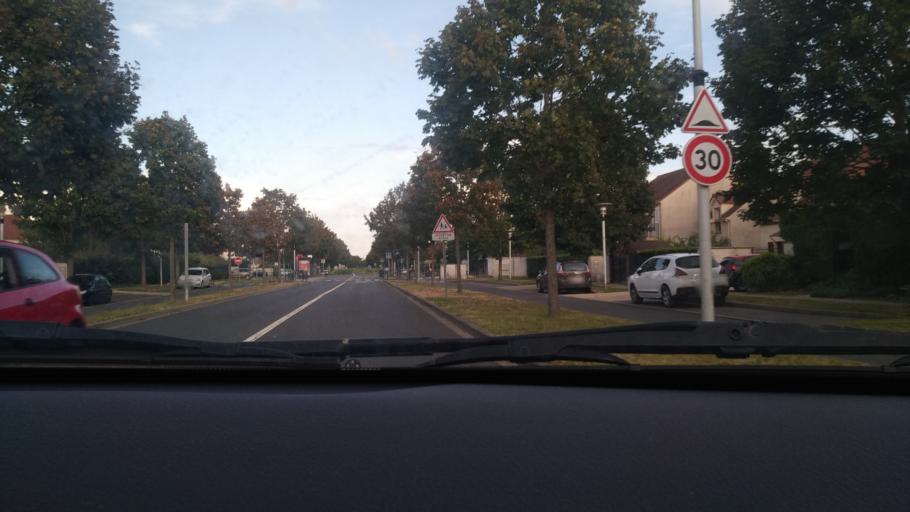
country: FR
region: Ile-de-France
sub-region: Departement de Seine-et-Marne
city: Lieusaint
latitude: 48.6375
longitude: 2.5511
